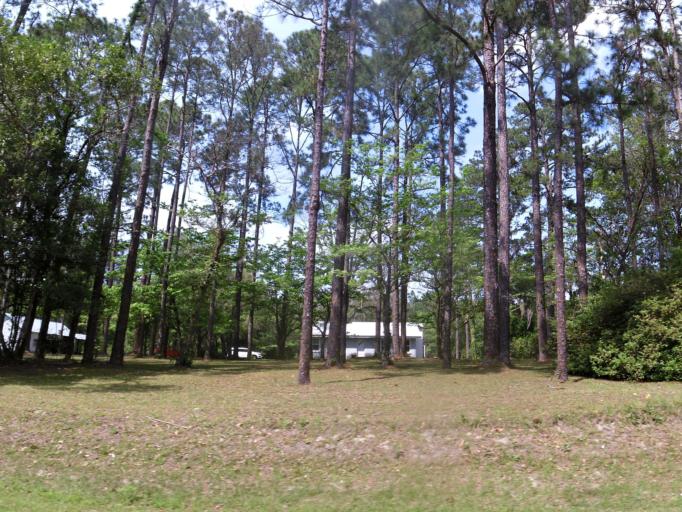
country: US
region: Georgia
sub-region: Camden County
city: Kingsland
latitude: 30.7814
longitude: -81.6934
